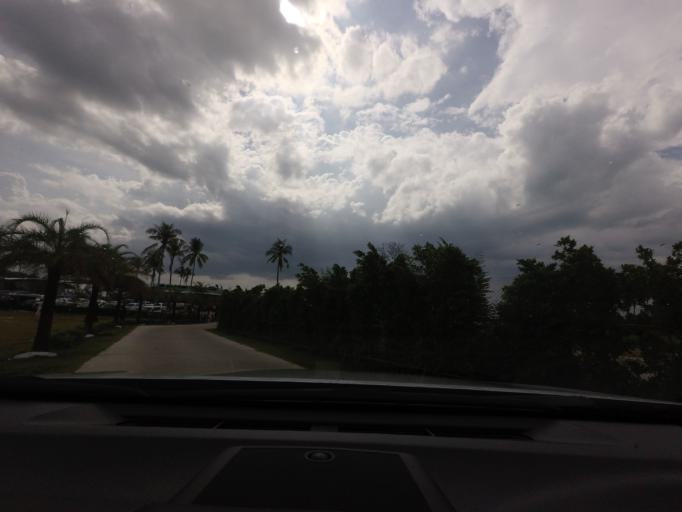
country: TH
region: Songkhla
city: Chana
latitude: 6.9543
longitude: 100.8356
